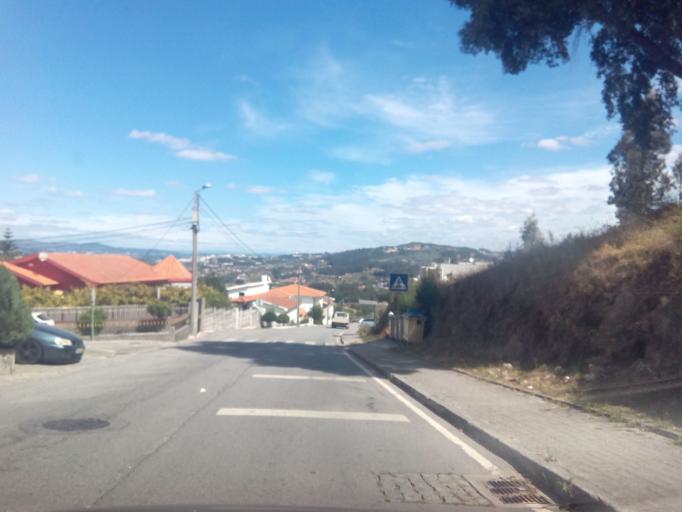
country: PT
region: Porto
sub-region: Paredes
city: Casteloes de Cepeda
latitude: 41.1566
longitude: -8.3162
